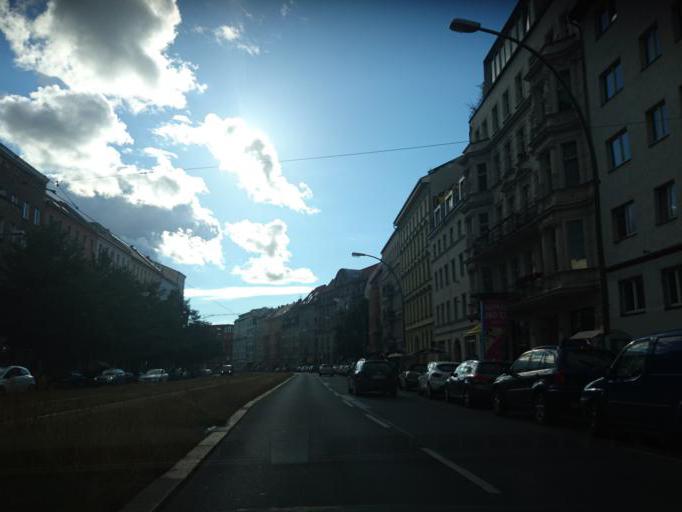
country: DE
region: Berlin
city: Berlin
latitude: 52.5296
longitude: 13.4054
